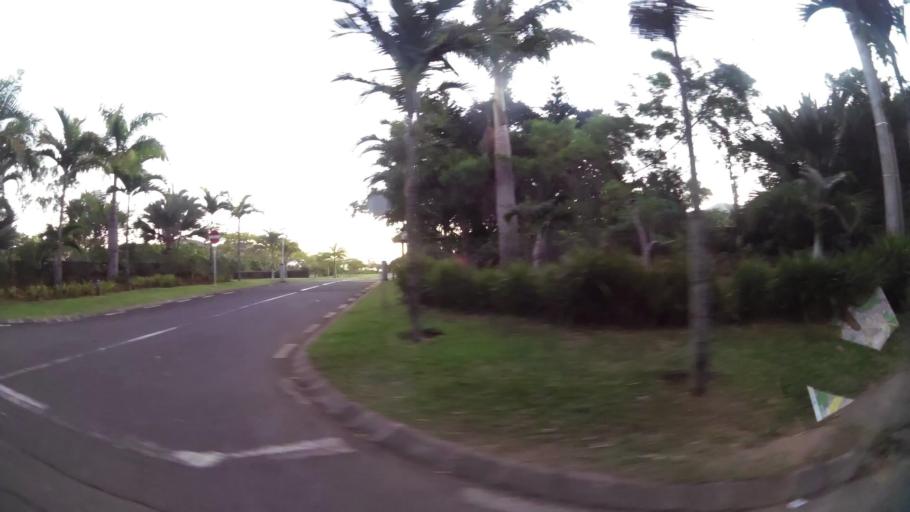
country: MU
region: Moka
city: Moka
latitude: -20.2202
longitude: 57.5010
